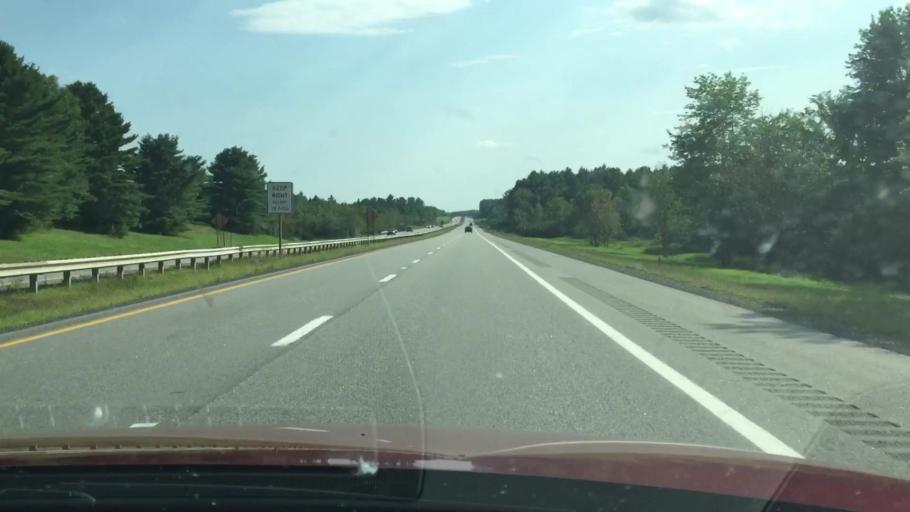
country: US
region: Maine
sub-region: Cumberland County
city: New Gloucester
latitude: 43.9127
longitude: -70.3393
